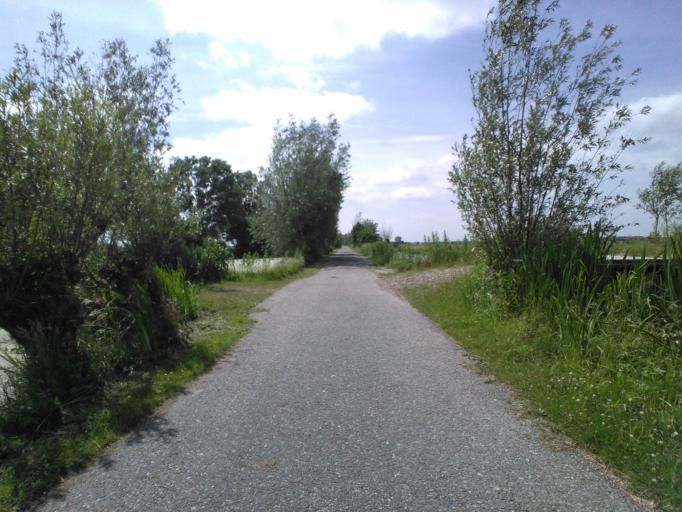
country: NL
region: South Holland
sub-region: Gemeente Gouda
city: Gouda
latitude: 51.9732
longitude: 4.6807
